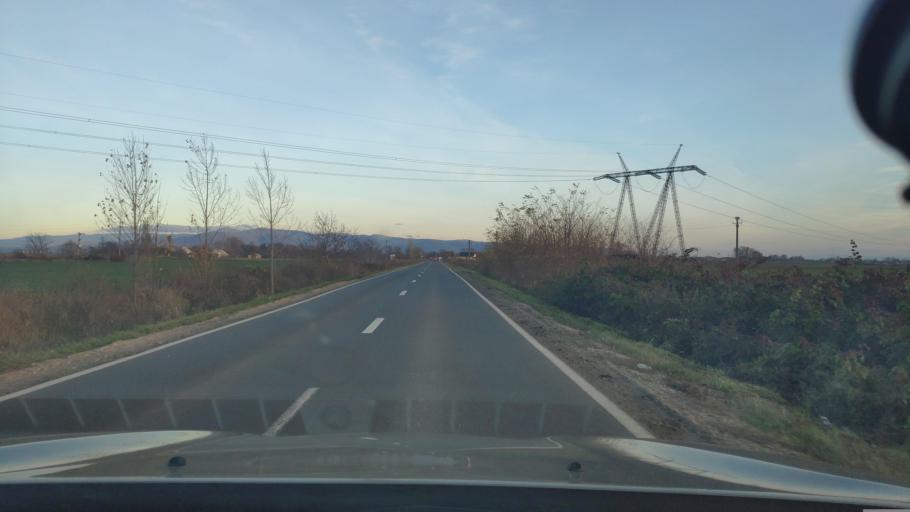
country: RO
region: Satu Mare
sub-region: Comuna Apa
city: Apa
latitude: 47.7671
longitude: 23.1749
